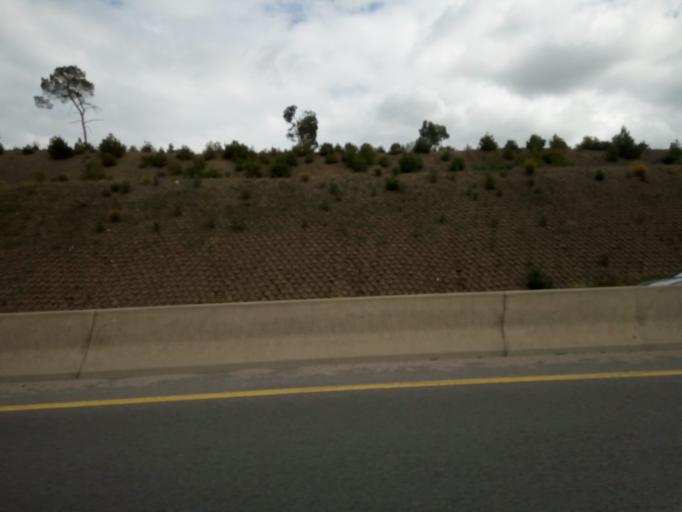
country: DZ
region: Bordj Bou Arreridj
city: Mansourah
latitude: 36.1933
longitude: 4.4344
